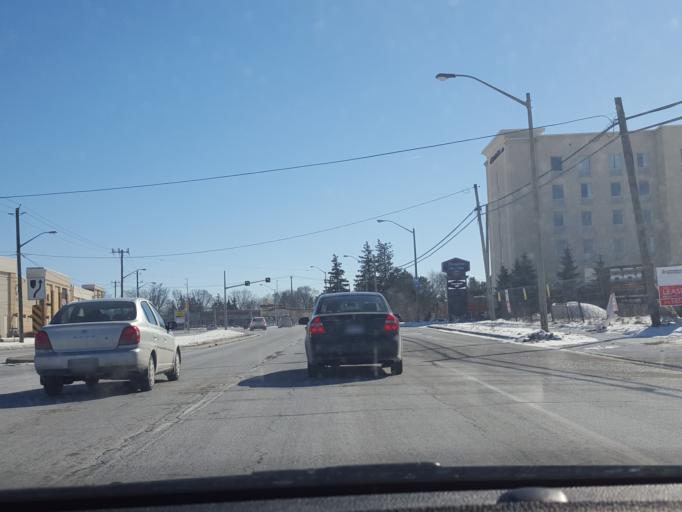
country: CA
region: Ontario
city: Cambridge
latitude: 43.4083
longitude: -80.3975
